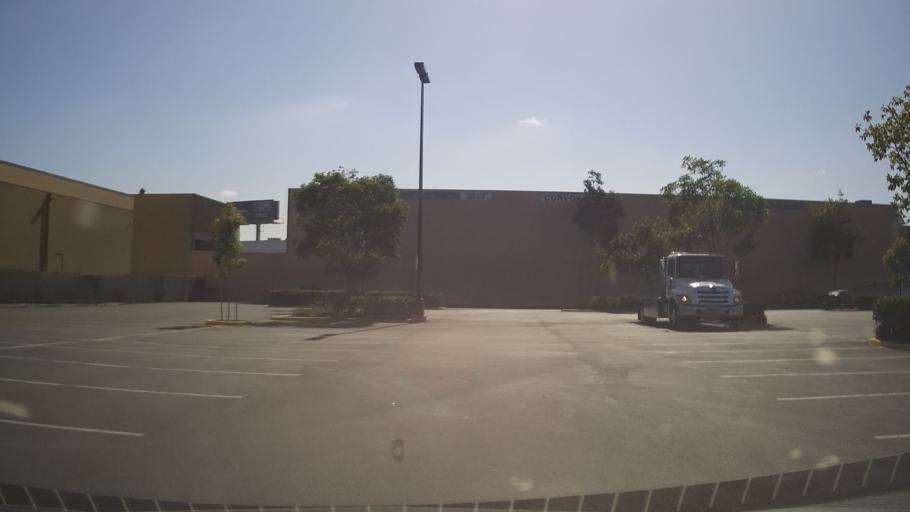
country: US
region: California
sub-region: San Diego County
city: San Diego
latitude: 32.8159
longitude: -117.1522
